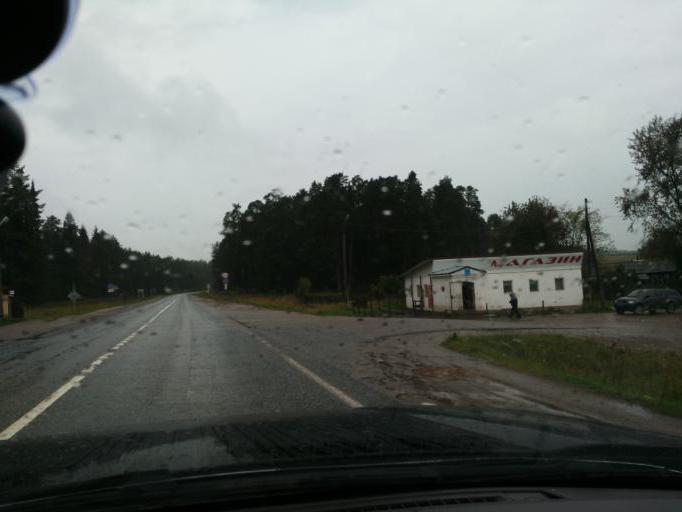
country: RU
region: Perm
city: Yugo-Kamskiy
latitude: 57.5581
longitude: 55.6836
